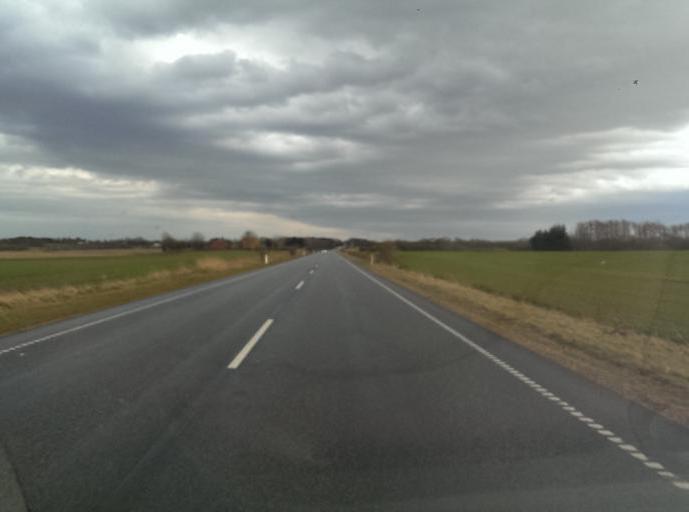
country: DK
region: South Denmark
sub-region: Esbjerg Kommune
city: Tjaereborg
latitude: 55.5027
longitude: 8.6071
